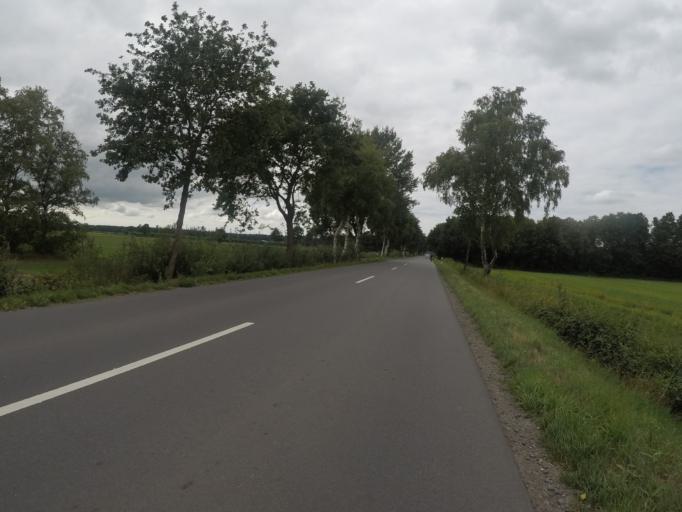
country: DE
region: Lower Saxony
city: Wingst
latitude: 53.7057
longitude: 9.0726
